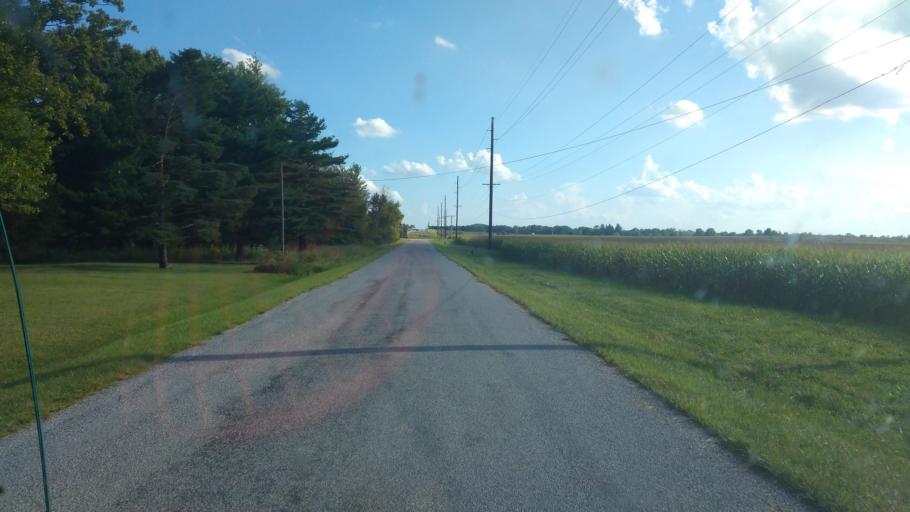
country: US
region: Ohio
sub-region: Crawford County
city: Crestline
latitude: 40.7688
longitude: -82.7458
